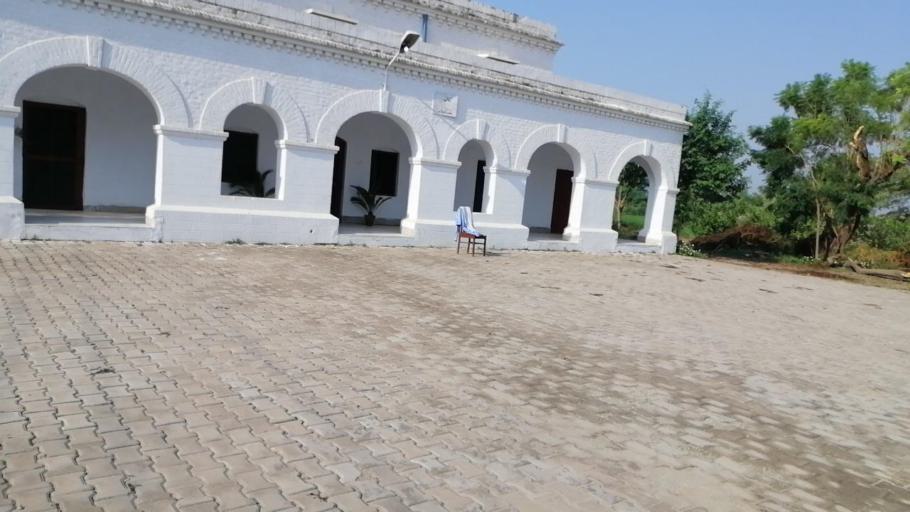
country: PK
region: Punjab
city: Kamalia
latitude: 30.6934
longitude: 72.7282
